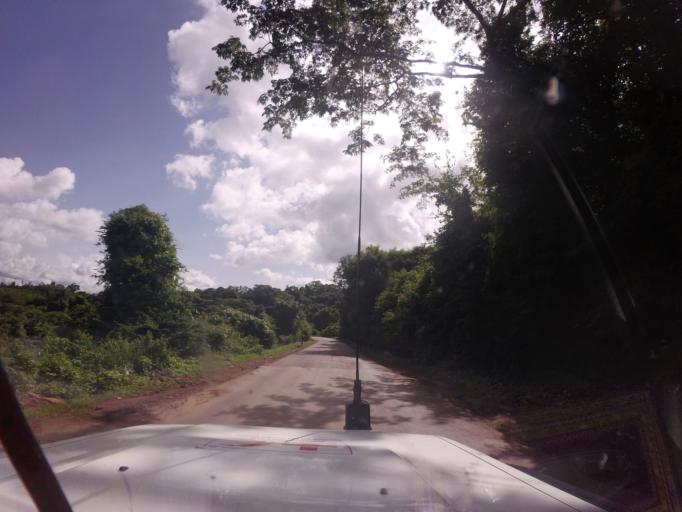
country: GN
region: Mamou
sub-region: Mamou Prefecture
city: Mamou
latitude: 10.3586
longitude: -12.1606
